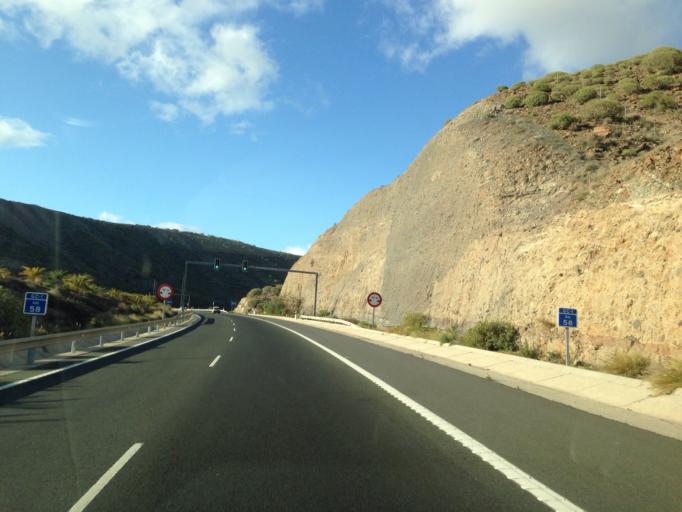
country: ES
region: Canary Islands
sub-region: Provincia de Las Palmas
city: Puerto Rico
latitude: 27.7815
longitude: -15.6778
